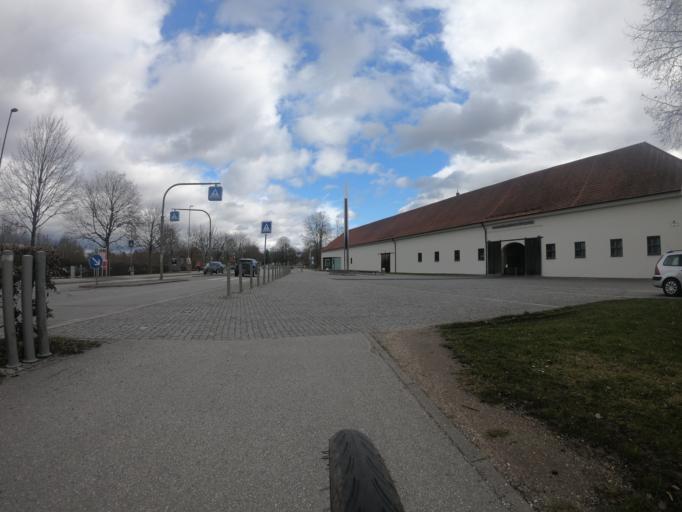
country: DE
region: Bavaria
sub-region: Upper Bavaria
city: Fuerstenfeldbruck
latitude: 48.1710
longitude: 11.2462
